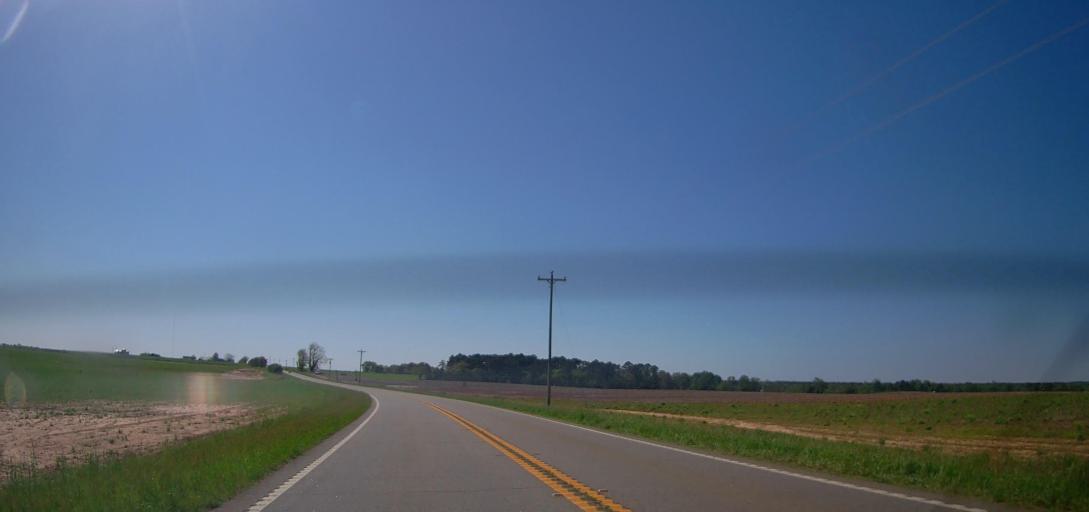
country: US
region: Georgia
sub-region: Dooly County
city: Unadilla
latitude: 32.2595
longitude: -83.6525
